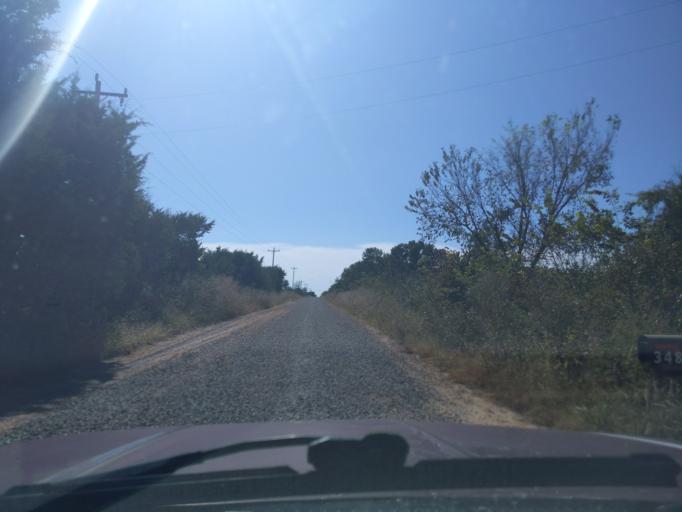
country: US
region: Oklahoma
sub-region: Creek County
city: Bristow
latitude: 35.6596
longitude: -96.4234
